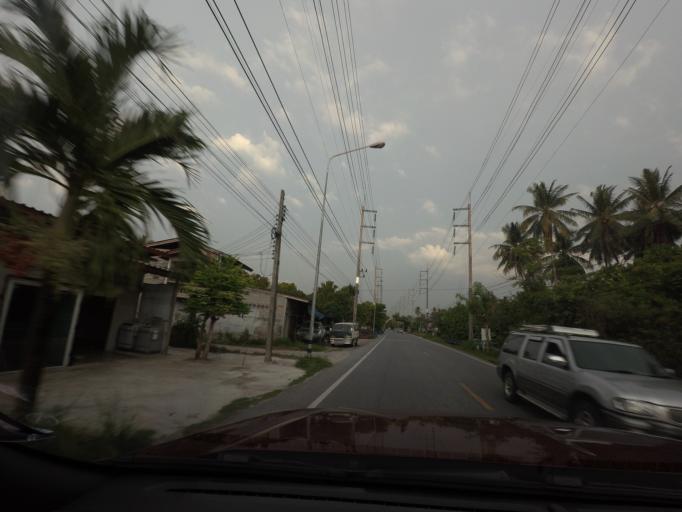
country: TH
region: Yala
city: Yala
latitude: 6.5709
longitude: 101.2041
